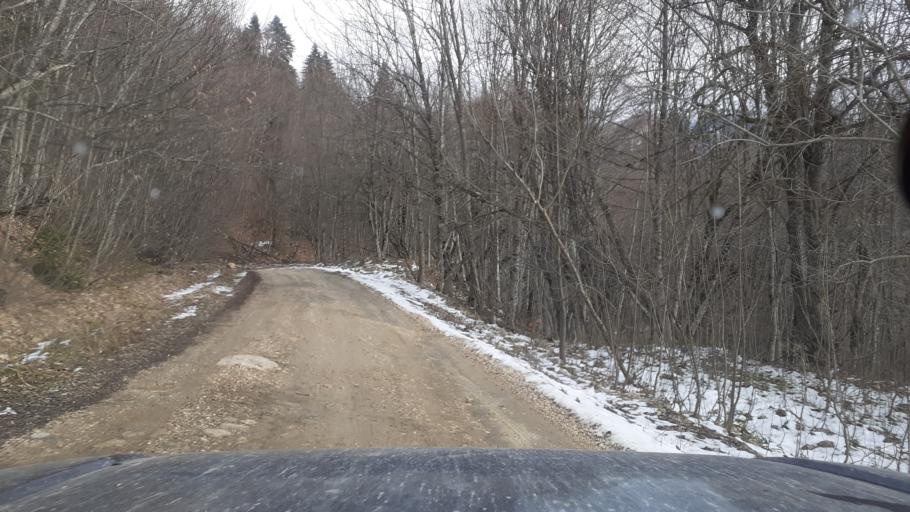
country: RU
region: Krasnodarskiy
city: Neftegorsk
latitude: 44.0709
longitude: 39.7689
